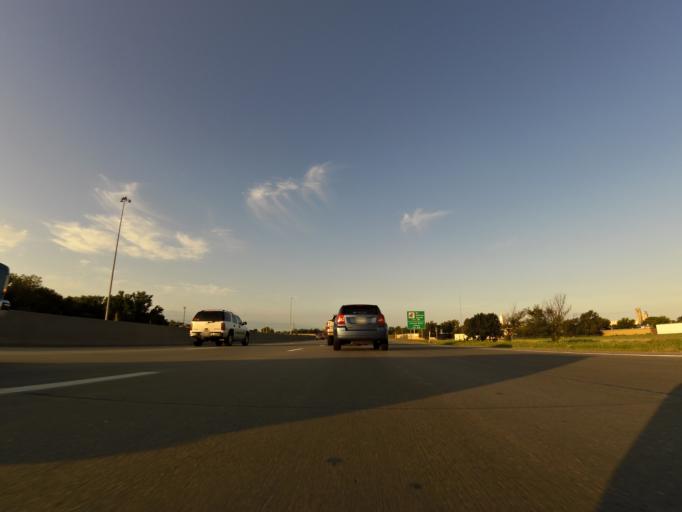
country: US
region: Kansas
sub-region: Sedgwick County
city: Wichita
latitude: 37.7192
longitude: -97.3206
